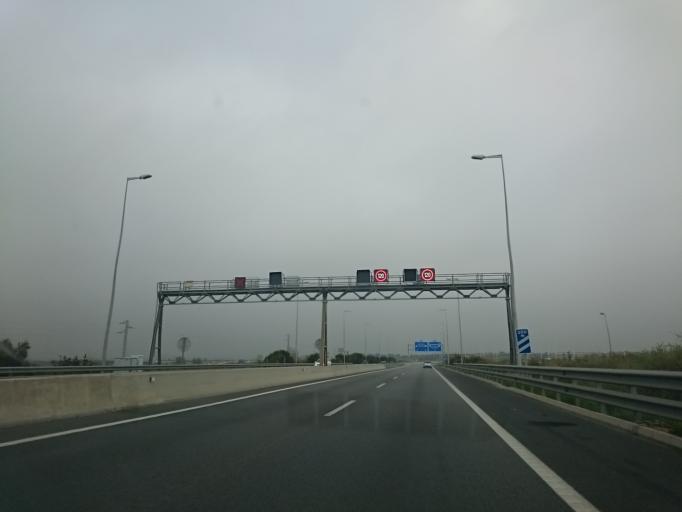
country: ES
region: Catalonia
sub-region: Provincia de Barcelona
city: Viladecans
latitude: 41.2893
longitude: 2.0517
